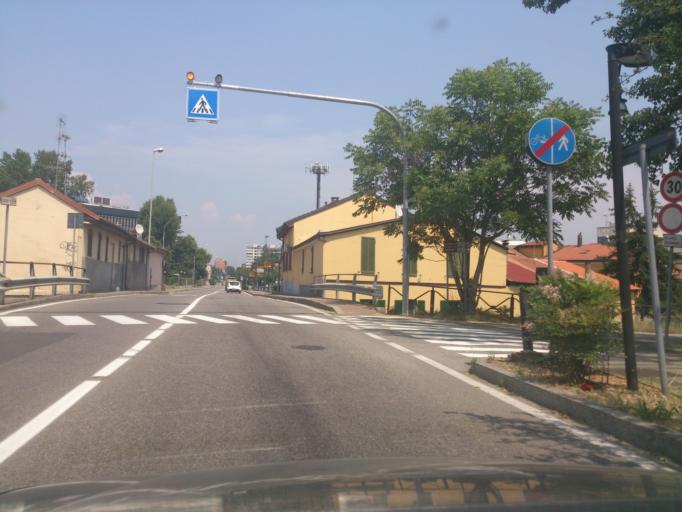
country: IT
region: Lombardy
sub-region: Citta metropolitana di Milano
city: Cologno Monzese
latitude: 45.5174
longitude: 9.2665
